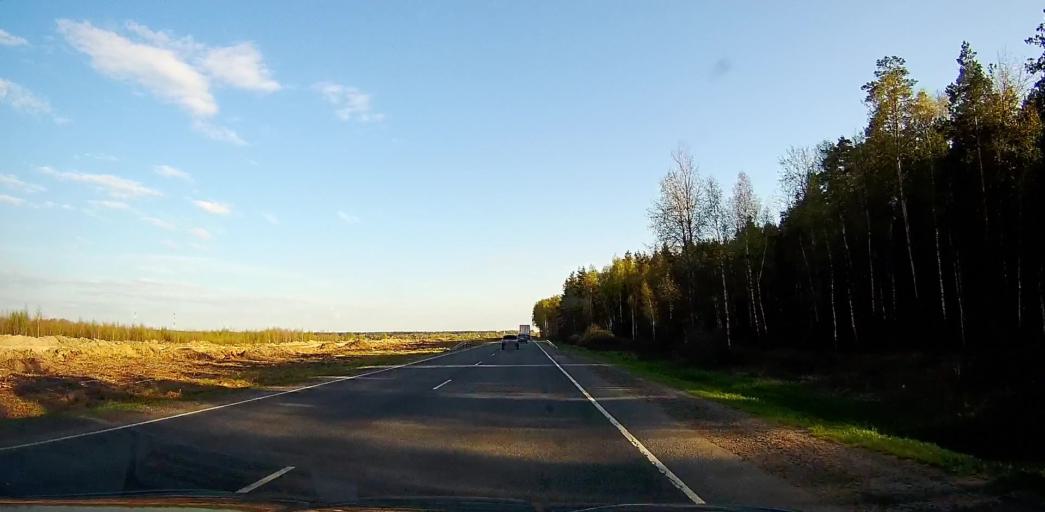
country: RU
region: Moskovskaya
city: Gzhel'
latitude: 55.5887
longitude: 38.3836
